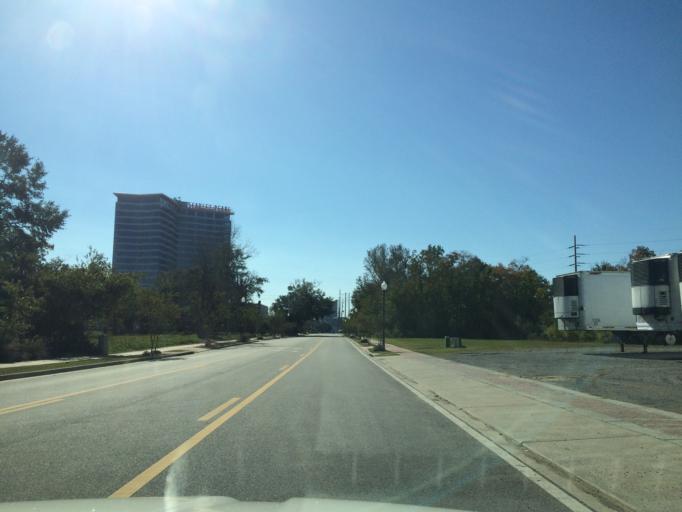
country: US
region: Mississippi
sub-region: Harrison County
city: D'Iberville
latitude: 30.4284
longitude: -88.8911
